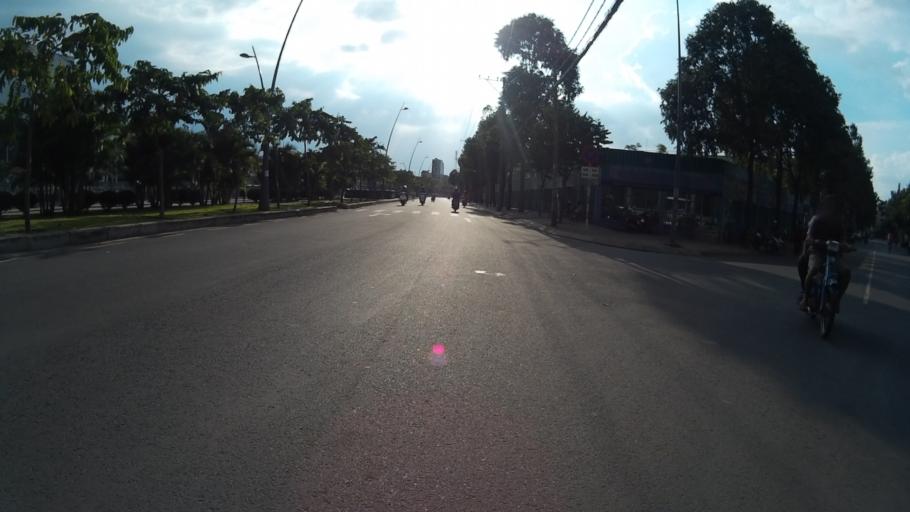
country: VN
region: Ho Chi Minh City
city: Quan Binh Thanh
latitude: 10.7959
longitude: 106.6888
